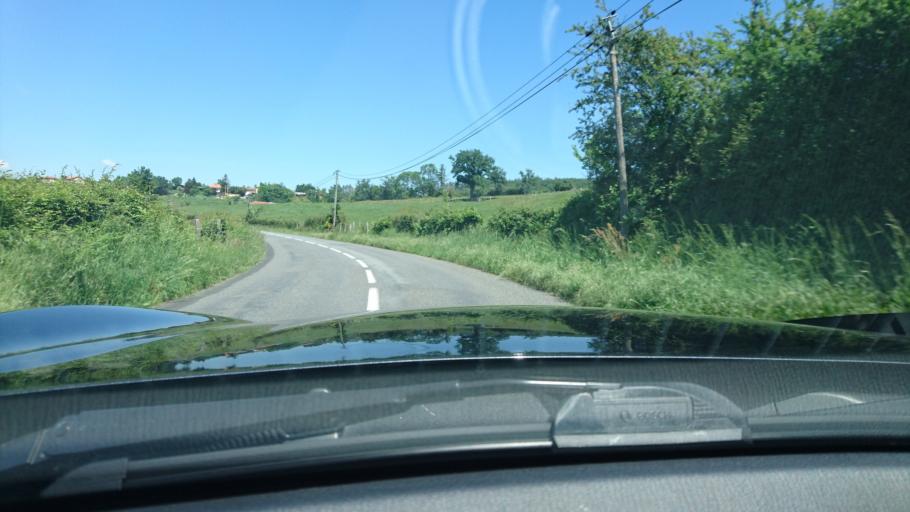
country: FR
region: Rhone-Alpes
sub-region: Departement de la Loire
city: Rozier-en-Donzy
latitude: 45.7894
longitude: 4.3044
